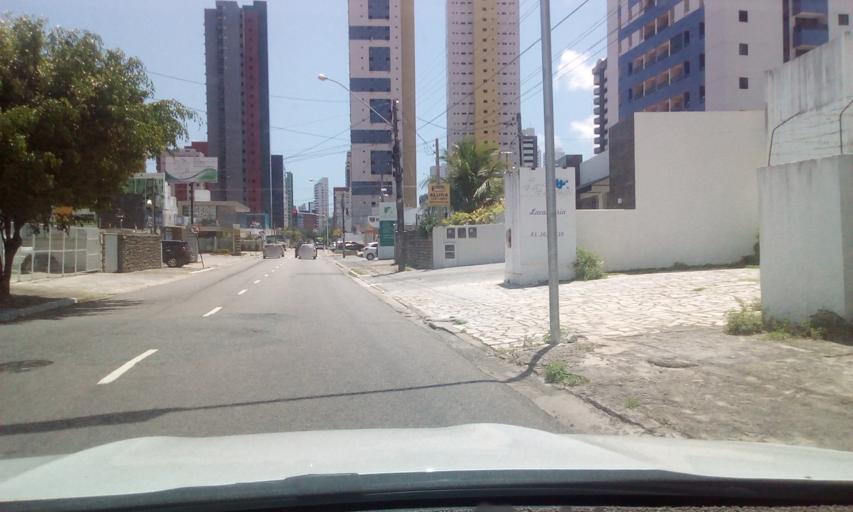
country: BR
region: Paraiba
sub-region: Joao Pessoa
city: Joao Pessoa
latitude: -7.1014
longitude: -34.8367
